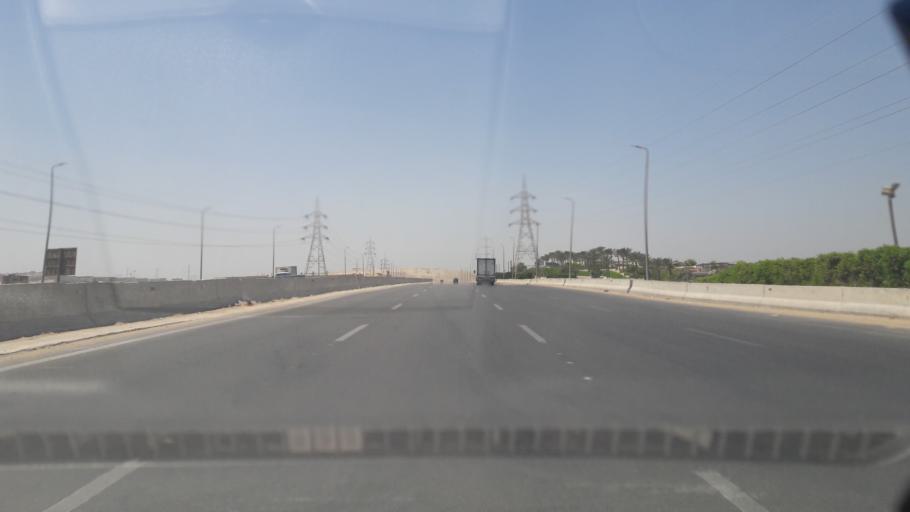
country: EG
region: Al Jizah
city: Al Jizah
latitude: 30.0056
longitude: 31.0882
